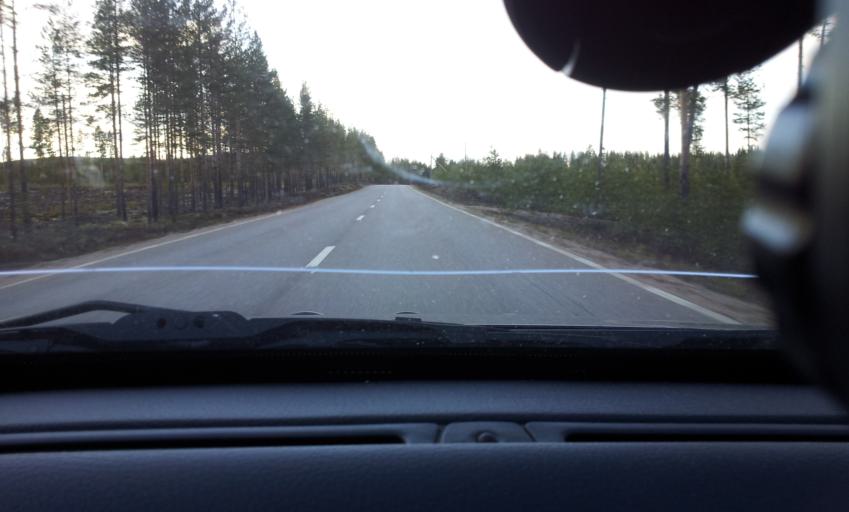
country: SE
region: Vaesternorrland
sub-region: Ange Kommun
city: Ange
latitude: 62.0641
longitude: 15.1106
